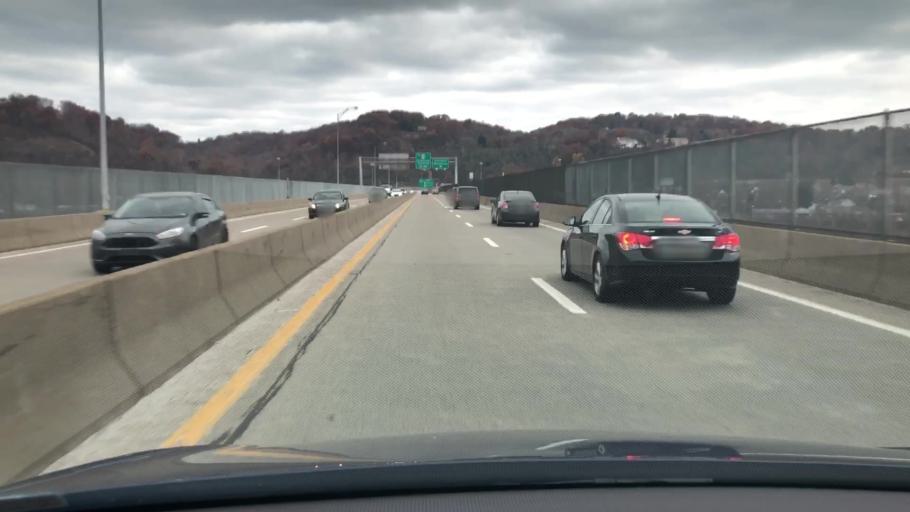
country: US
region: Pennsylvania
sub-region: Allegheny County
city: Aspinwall
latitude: 40.4881
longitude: -79.9125
